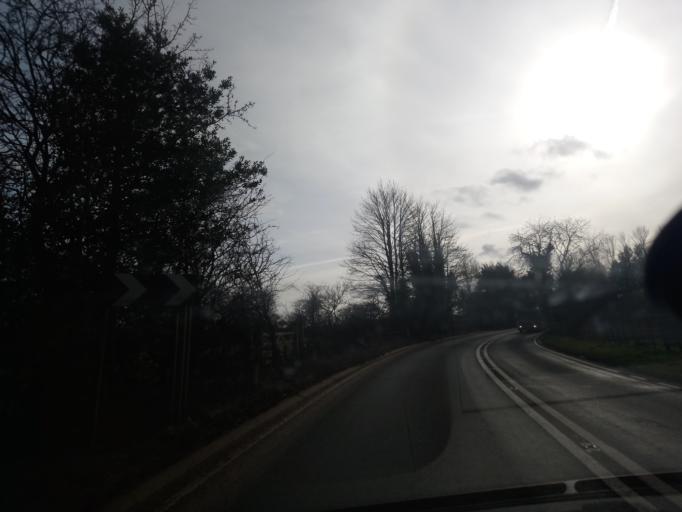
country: GB
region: England
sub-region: Shropshire
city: Prees
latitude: 52.8790
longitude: -2.6540
